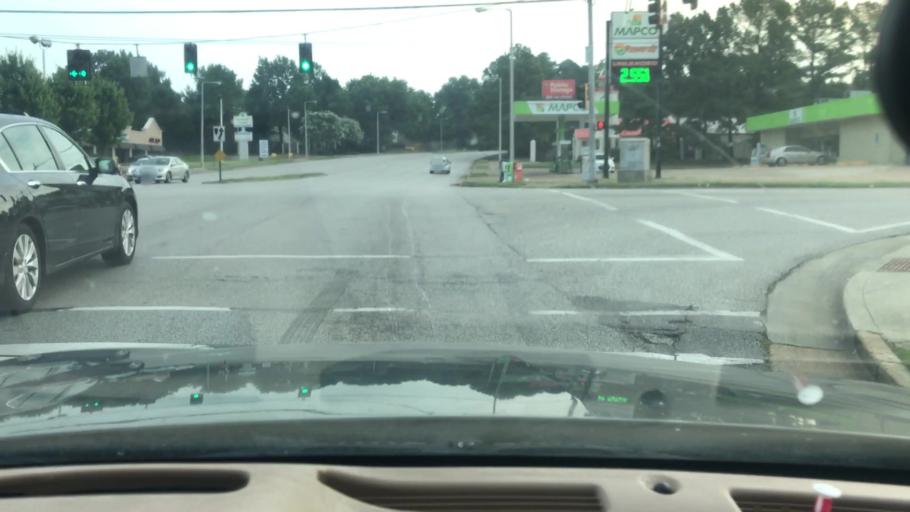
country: US
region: Tennessee
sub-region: Shelby County
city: Bartlett
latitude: 35.1826
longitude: -89.8713
